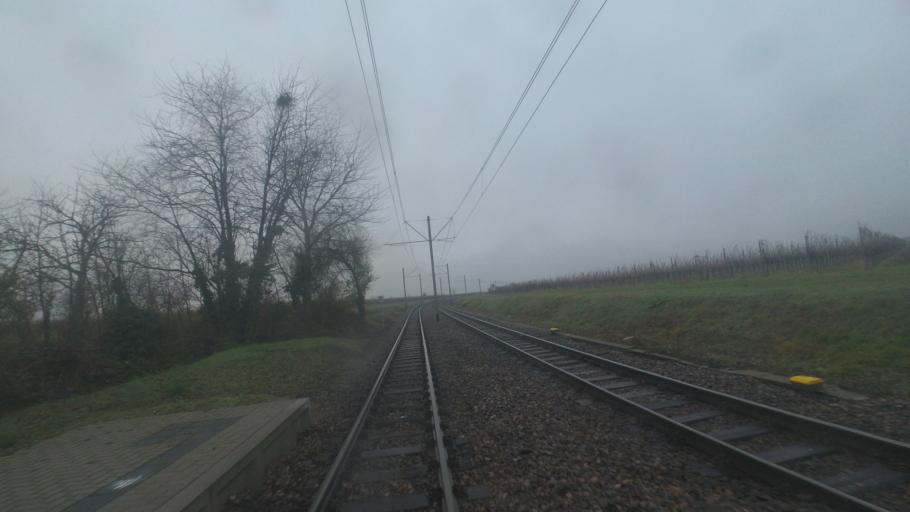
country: DE
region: Rheinland-Pfalz
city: Friedelsheim
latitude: 49.4584
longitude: 8.2240
